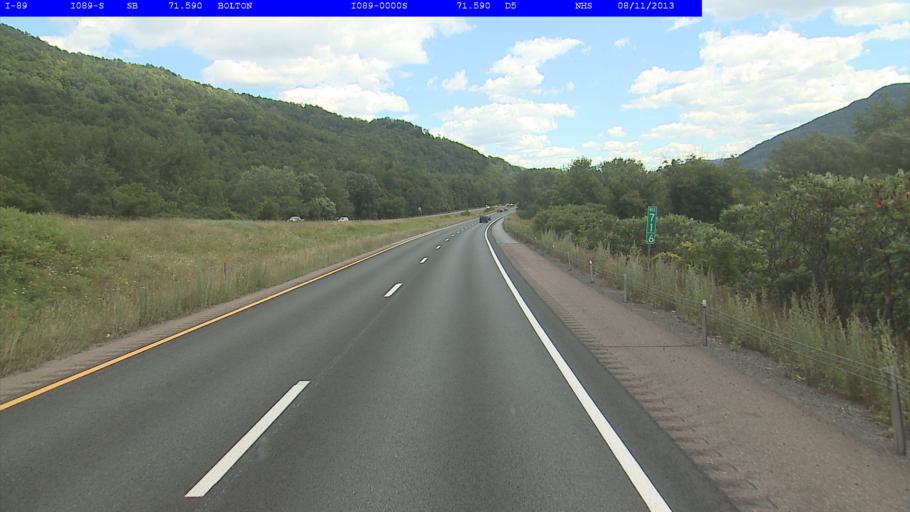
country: US
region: Vermont
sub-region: Washington County
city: Waterbury
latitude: 44.3779
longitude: -72.8984
